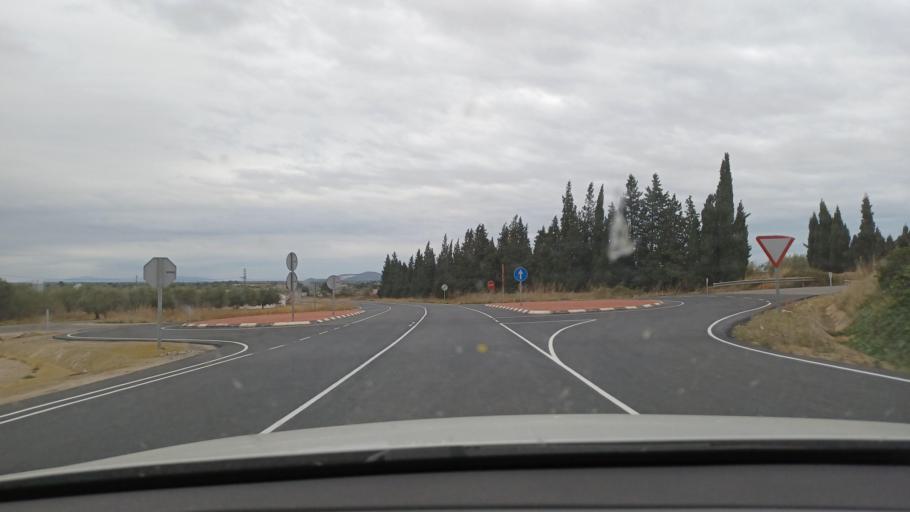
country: ES
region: Valencia
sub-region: Provincia de Castello
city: Traiguera
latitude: 40.5335
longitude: 0.3044
